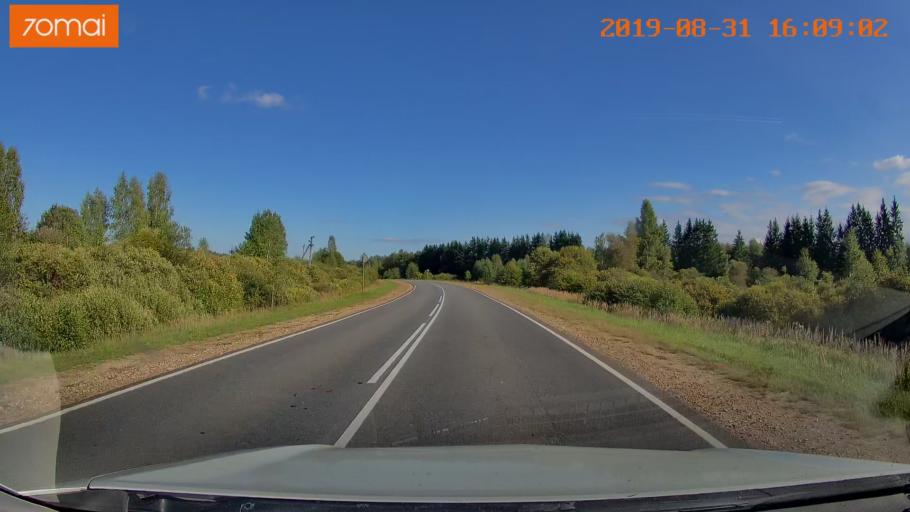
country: RU
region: Kaluga
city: Yukhnov
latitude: 54.5904
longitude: 35.3880
